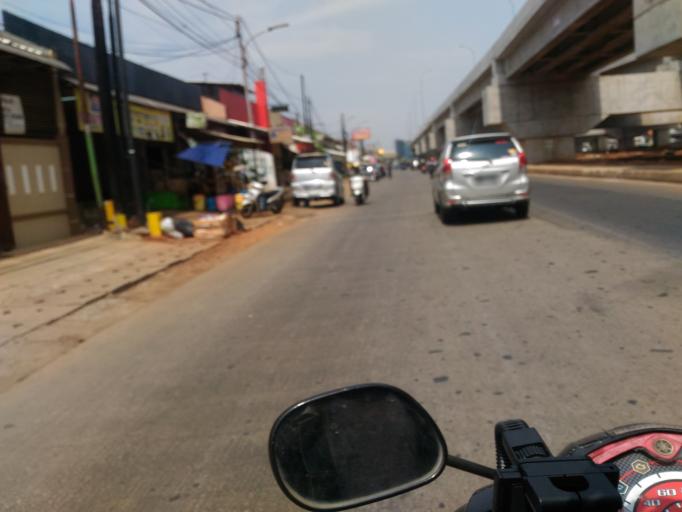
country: ID
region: Jakarta Raya
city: Jakarta
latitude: -6.2396
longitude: 106.8852
